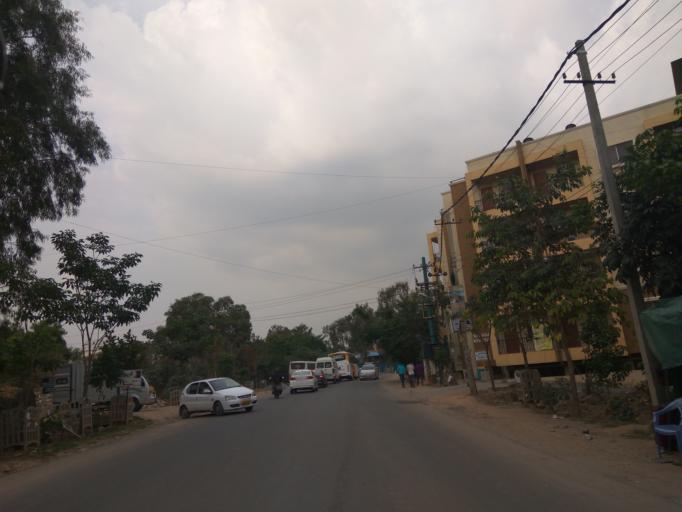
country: IN
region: Karnataka
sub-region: Bangalore Urban
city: Bangalore
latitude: 12.9732
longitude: 77.7023
